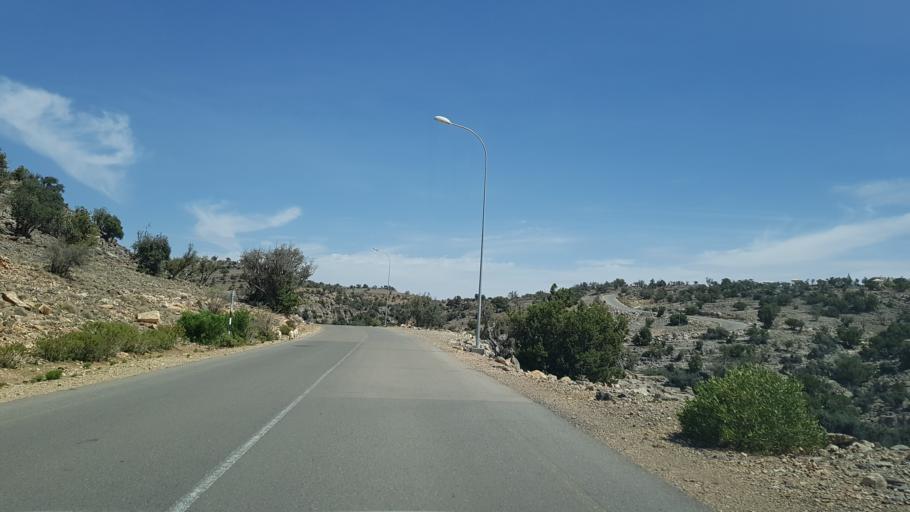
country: OM
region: Al Batinah
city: Bayt al `Awabi
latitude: 23.1369
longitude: 57.5953
